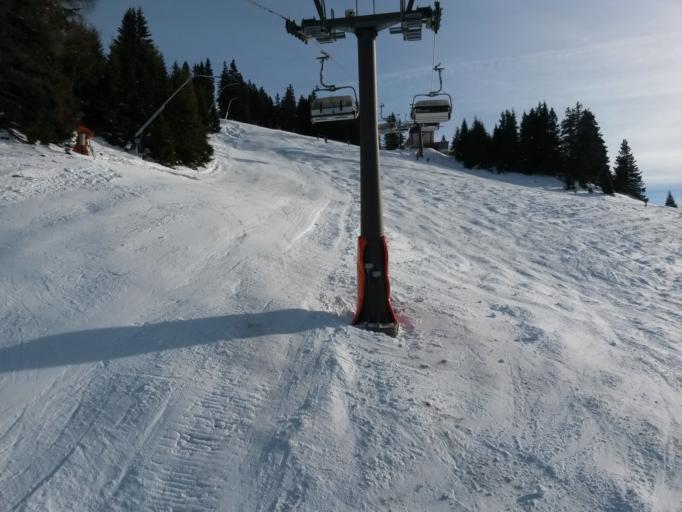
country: AT
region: Salzburg
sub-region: Politischer Bezirk Sankt Johann im Pongau
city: Dorfgastein
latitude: 47.2349
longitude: 13.1341
